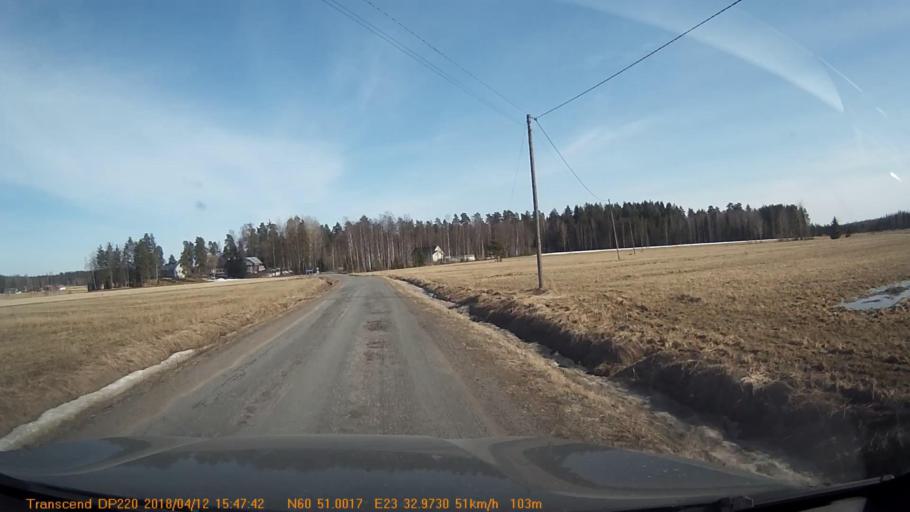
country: FI
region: Haeme
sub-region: Forssa
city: Forssa
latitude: 60.8499
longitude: 23.5499
